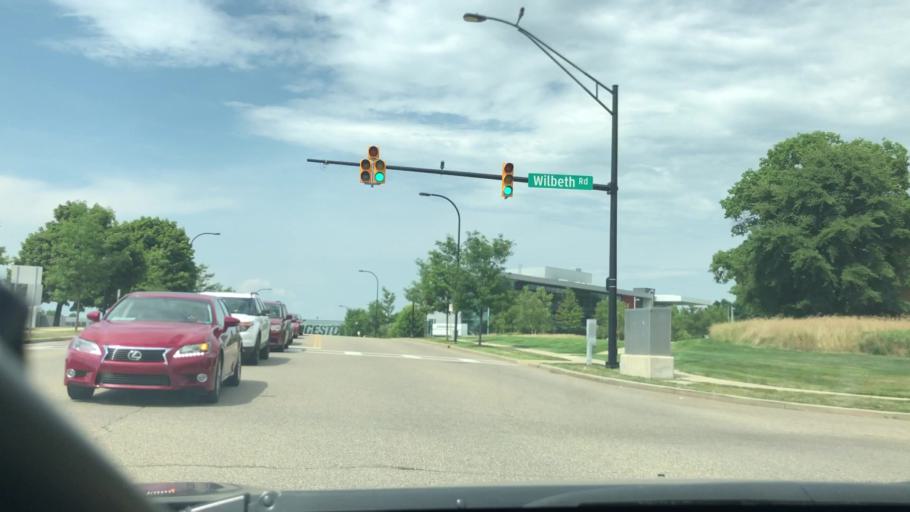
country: US
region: Ohio
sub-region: Summit County
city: Portage Lakes
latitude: 41.0400
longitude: -81.5268
